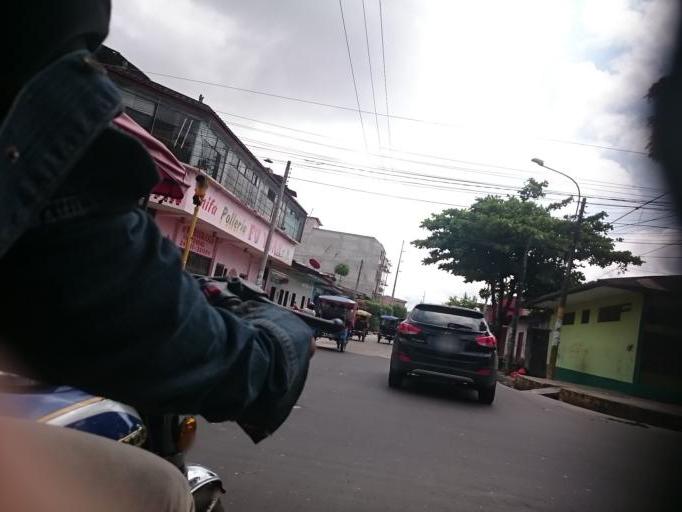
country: PE
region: Loreto
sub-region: Provincia de Maynas
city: Iquitos
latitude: -3.7454
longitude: -73.2500
